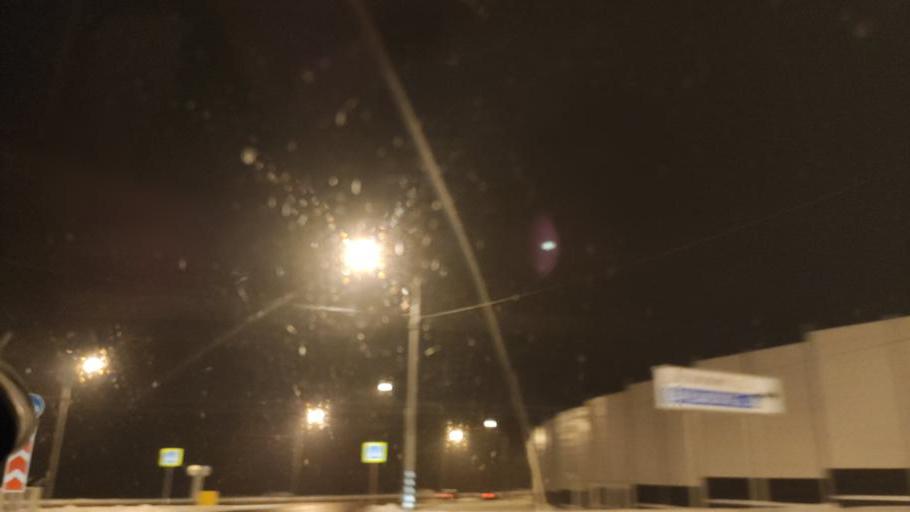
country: RU
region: Moscow
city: Annino
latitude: 55.5259
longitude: 37.6244
